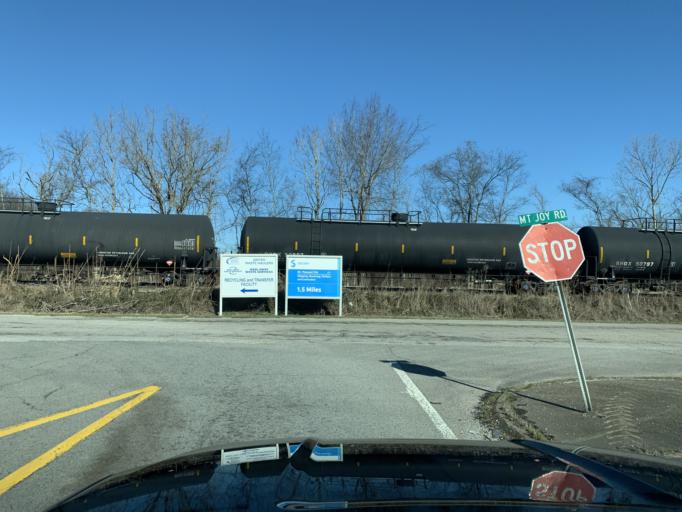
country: US
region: Tennessee
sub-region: Maury County
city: Mount Pleasant
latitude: 35.5207
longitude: -87.2247
